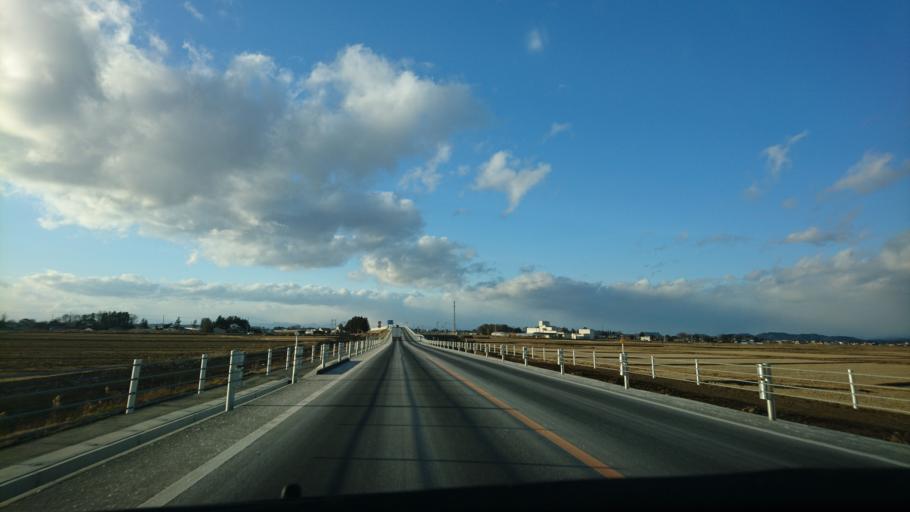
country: JP
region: Miyagi
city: Wakuya
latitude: 38.6808
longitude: 141.2550
